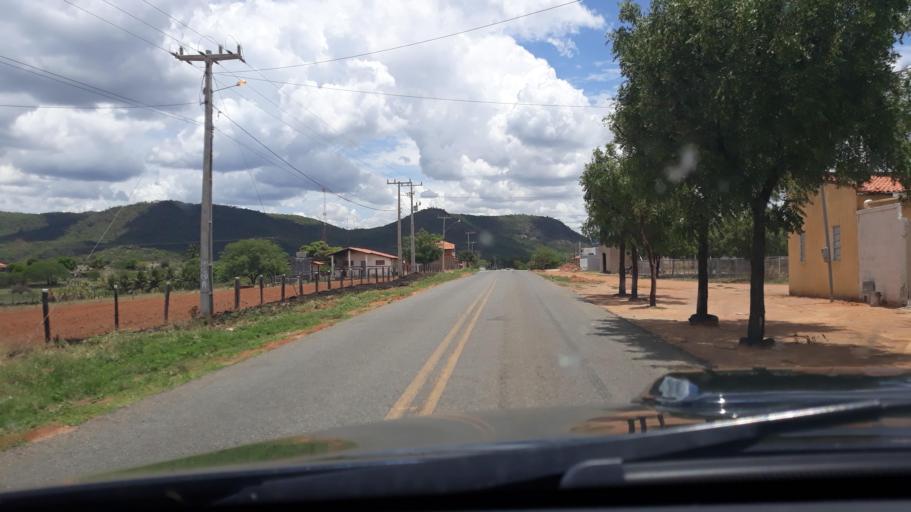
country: BR
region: Bahia
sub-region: Guanambi
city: Guanambi
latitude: -14.1126
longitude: -42.8619
